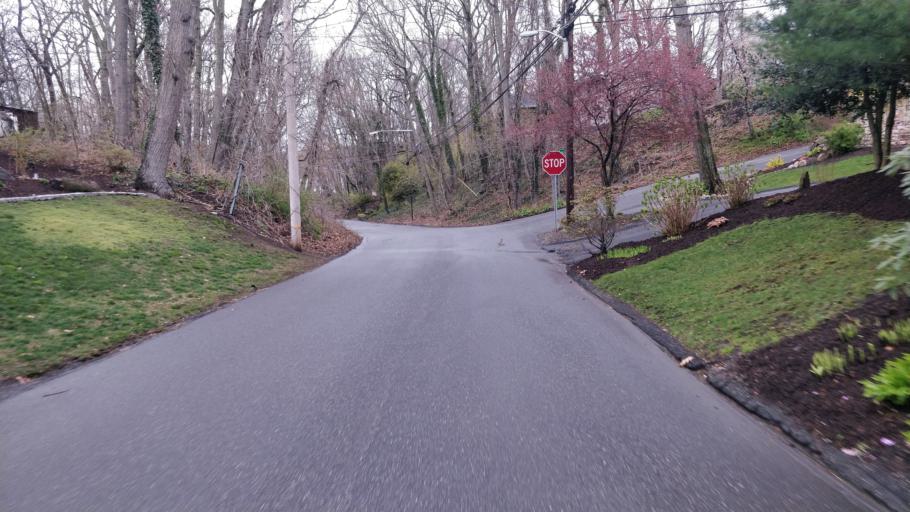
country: US
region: New York
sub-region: Suffolk County
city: Port Jefferson
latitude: 40.9508
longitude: -73.0839
